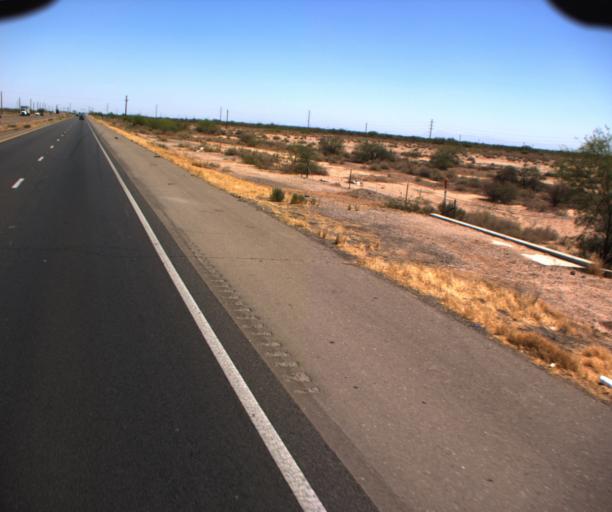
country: US
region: Arizona
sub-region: Pinal County
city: Maricopa
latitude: 33.1156
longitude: -112.0215
